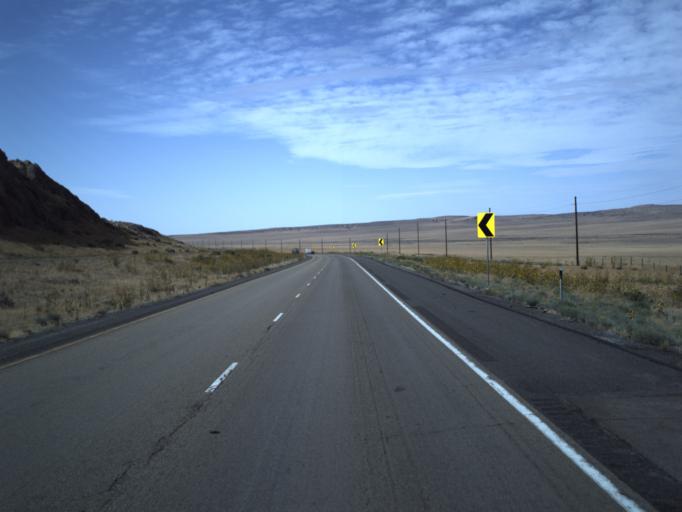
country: US
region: Utah
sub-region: Tooele County
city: Grantsville
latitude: 40.8134
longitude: -112.9236
